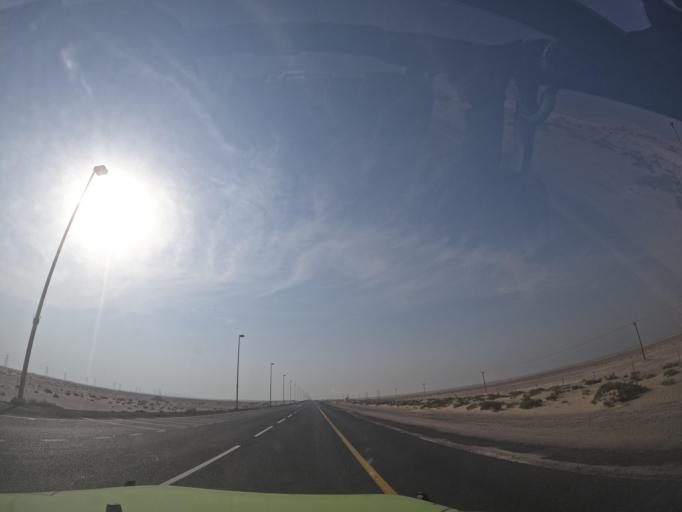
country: AE
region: Dubai
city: Dubai
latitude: 24.7642
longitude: 55.0956
